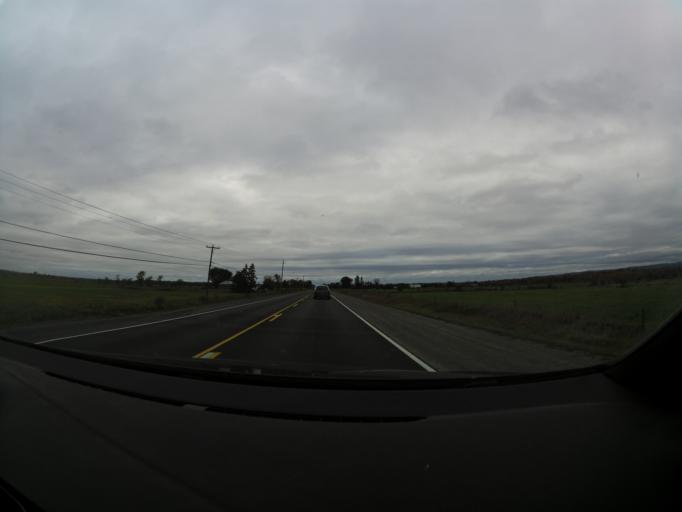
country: CA
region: Ontario
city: Bells Corners
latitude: 45.4275
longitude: -76.0275
